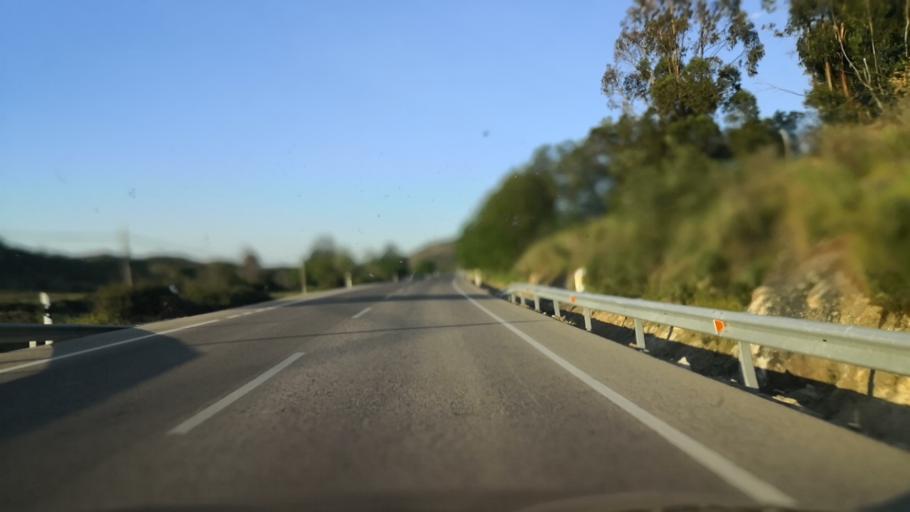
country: ES
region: Extremadura
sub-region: Provincia de Caceres
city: Valencia de Alcantara
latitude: 39.3721
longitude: -7.2618
